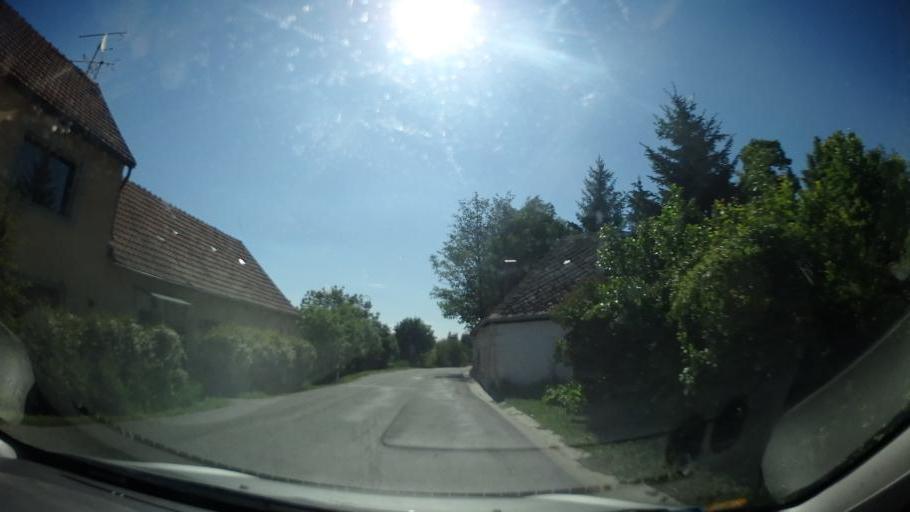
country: CZ
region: South Moravian
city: Velke Opatovice
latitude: 49.6246
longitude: 16.6044
